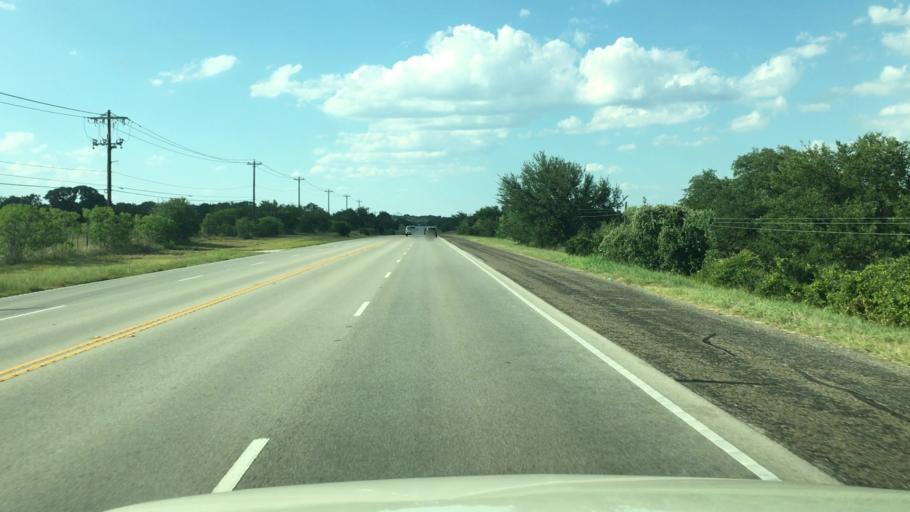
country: US
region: Texas
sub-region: Blanco County
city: Johnson City
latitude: 30.3542
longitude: -98.3781
